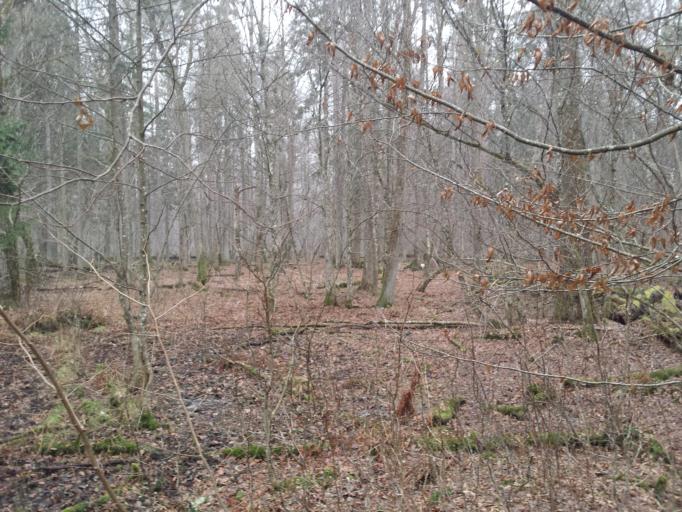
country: PL
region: Podlasie
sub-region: Powiat hajnowski
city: Bialowieza
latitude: 52.7214
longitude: 23.8383
